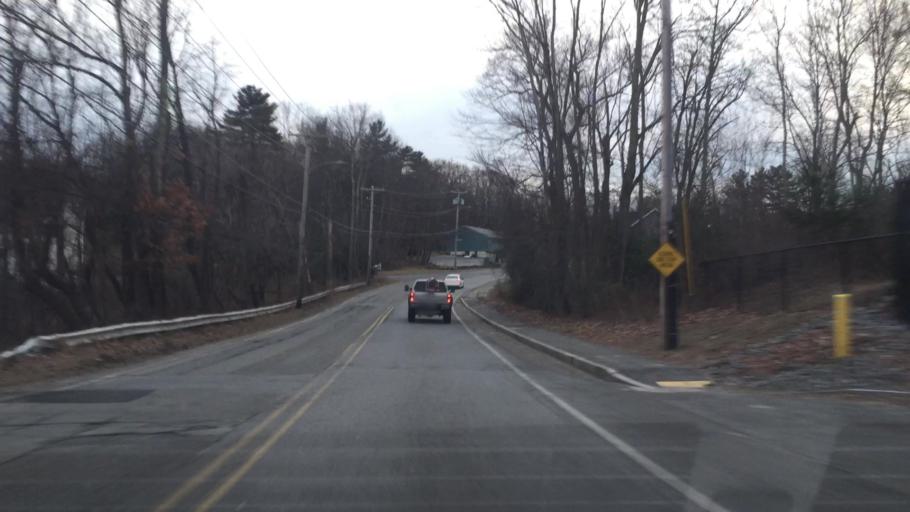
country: US
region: New Hampshire
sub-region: Hillsborough County
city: Pelham
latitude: 42.6944
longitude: -71.3503
